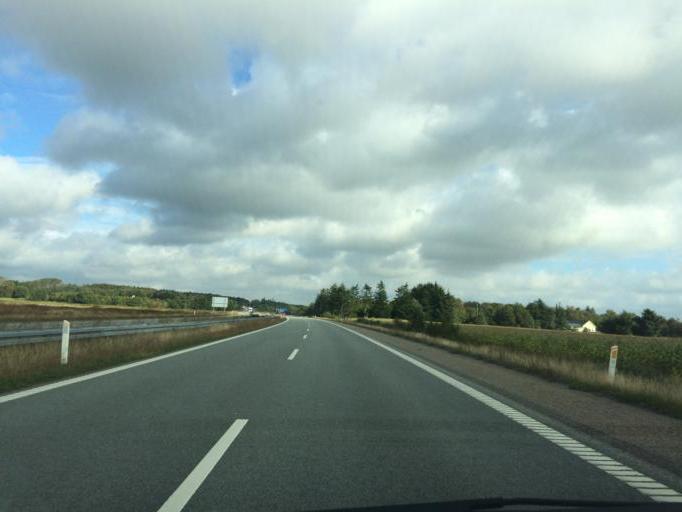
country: DK
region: North Denmark
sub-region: Alborg Kommune
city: Vodskov
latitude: 57.1067
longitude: 10.0487
